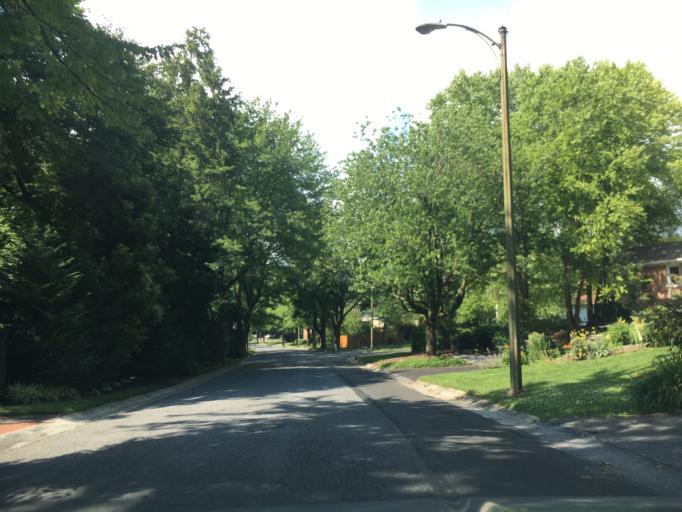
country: US
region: Pennsylvania
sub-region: Berks County
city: Wyomissing
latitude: 40.3222
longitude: -75.9619
